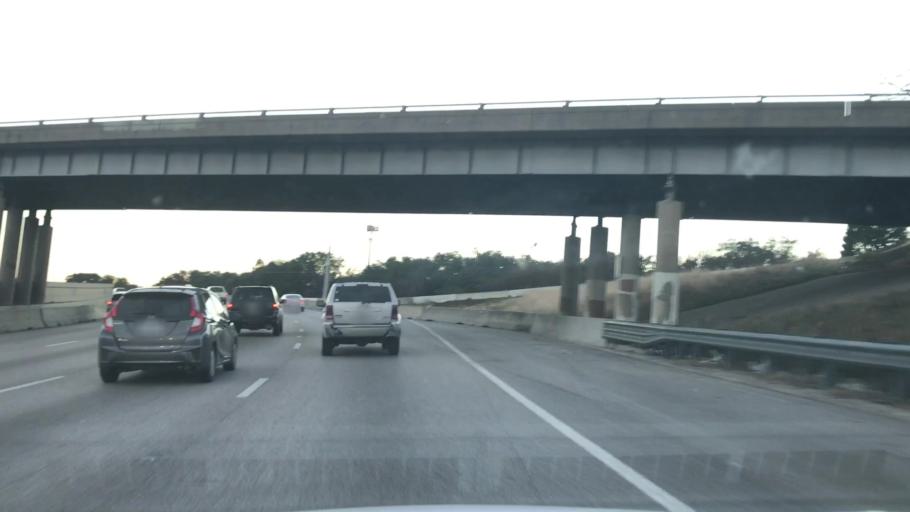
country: US
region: Texas
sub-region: Dallas County
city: Dallas
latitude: 32.7396
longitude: -96.8234
